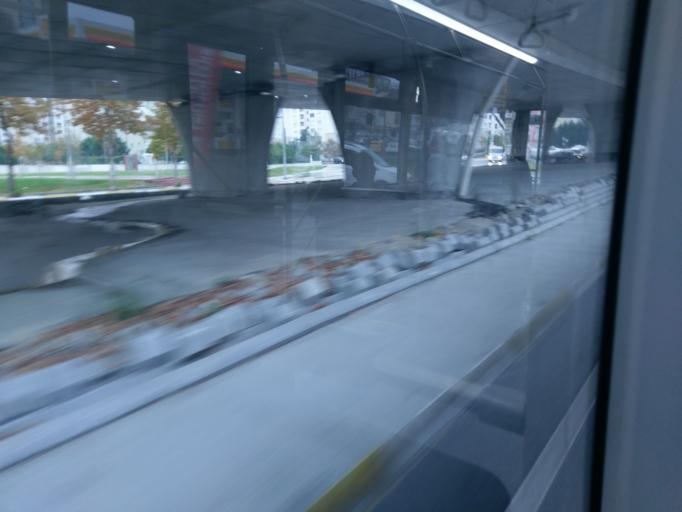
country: TR
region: Istanbul
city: Mahmutbey
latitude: 41.0341
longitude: 28.7680
